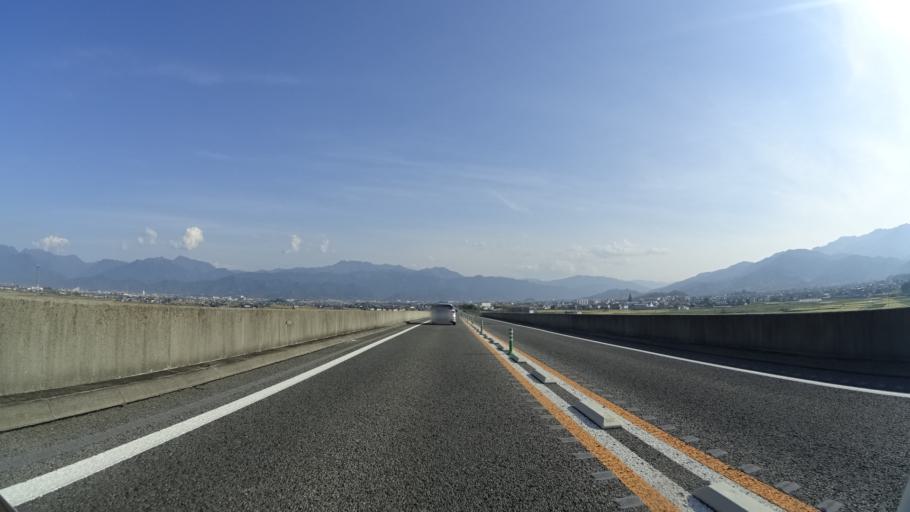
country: JP
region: Ehime
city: Saijo
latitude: 33.9488
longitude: 133.0693
